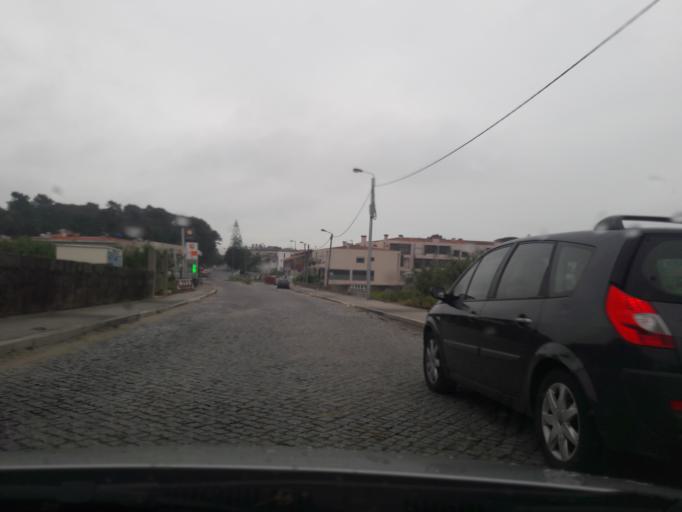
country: PT
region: Porto
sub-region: Vila do Conde
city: Arvore
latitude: 41.3380
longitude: -8.7341
